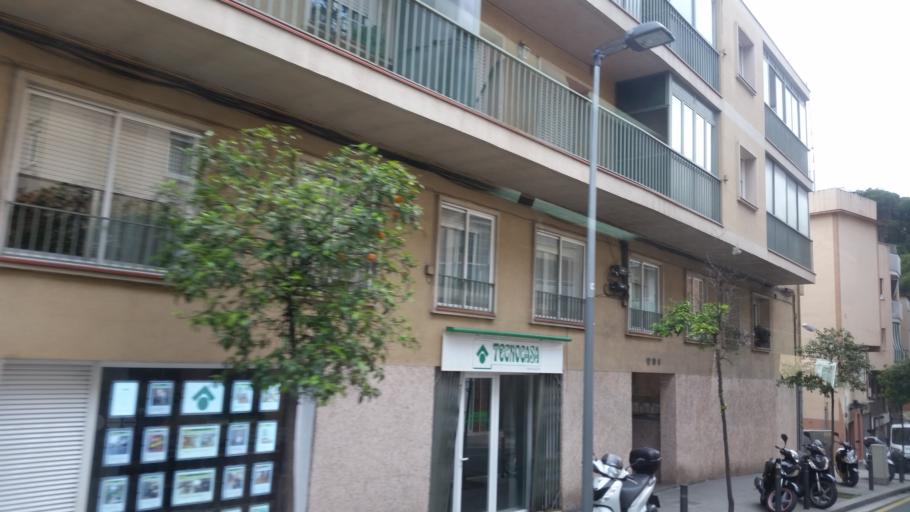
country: ES
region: Catalonia
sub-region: Provincia de Barcelona
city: Horta-Guinardo
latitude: 41.4203
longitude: 2.1502
